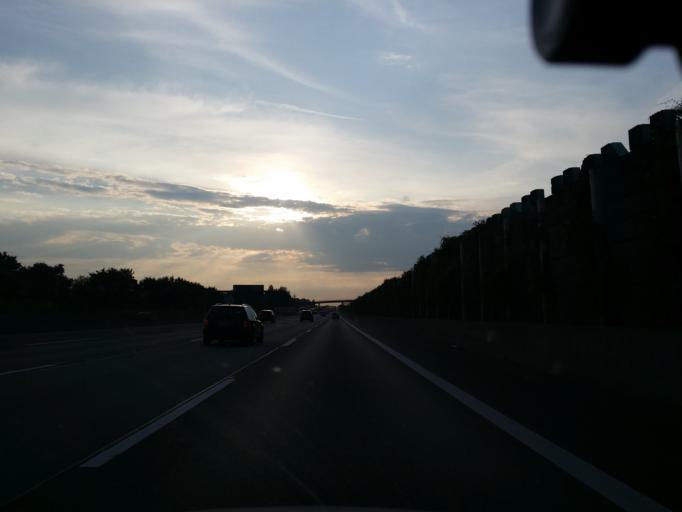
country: DE
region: Hesse
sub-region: Regierungsbezirk Darmstadt
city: Florsheim
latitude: 50.0358
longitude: 8.4384
